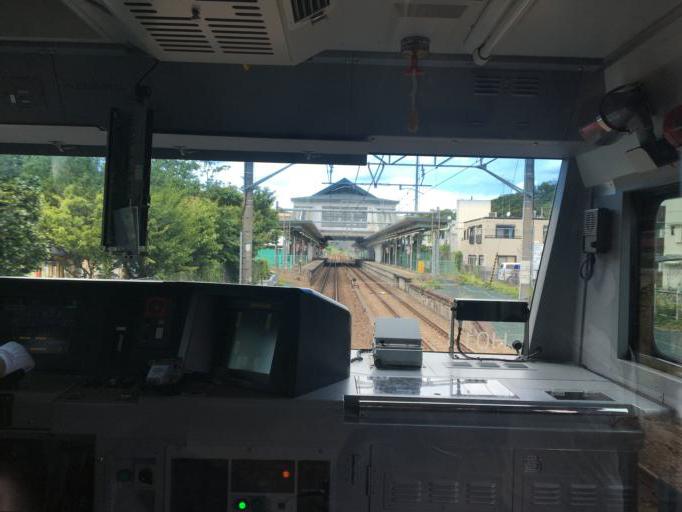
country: JP
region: Tokyo
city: Hachioji
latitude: 35.6058
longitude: 139.3317
